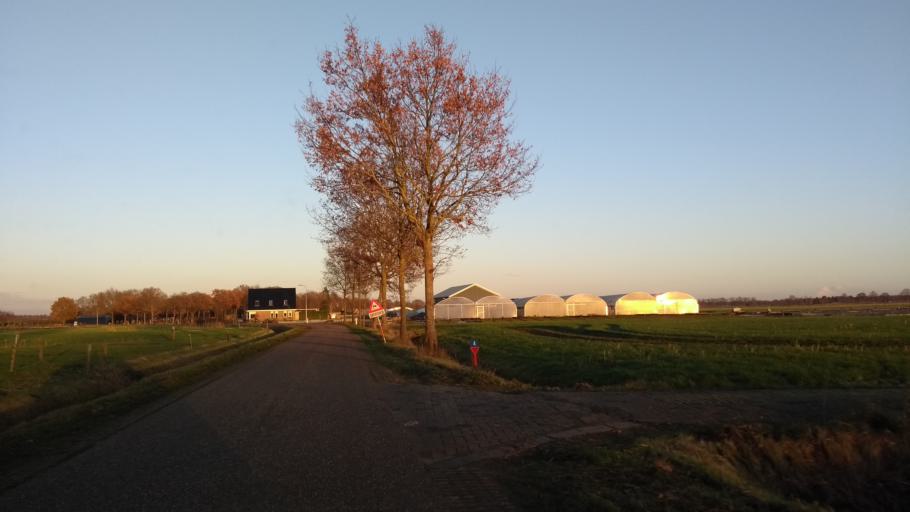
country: NL
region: Overijssel
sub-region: Gemeente Staphorst
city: Staphorst
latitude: 52.5997
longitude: 6.2908
